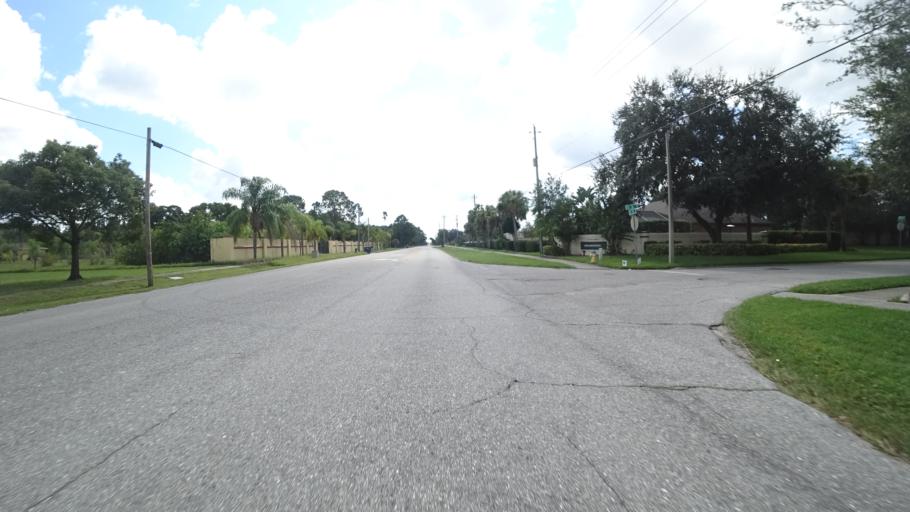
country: US
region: Florida
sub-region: Manatee County
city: Samoset
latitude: 27.4376
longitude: -82.5219
